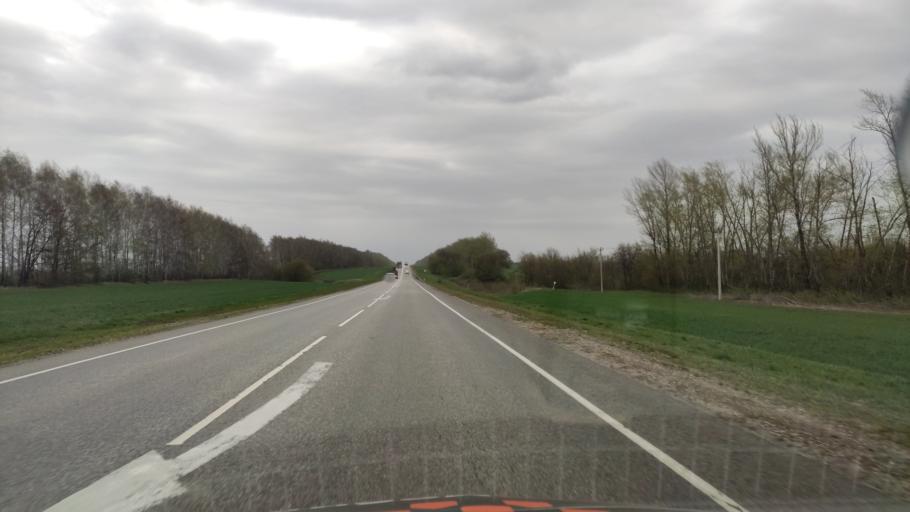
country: RU
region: Kursk
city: Gorshechnoye
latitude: 51.5492
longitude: 38.1467
